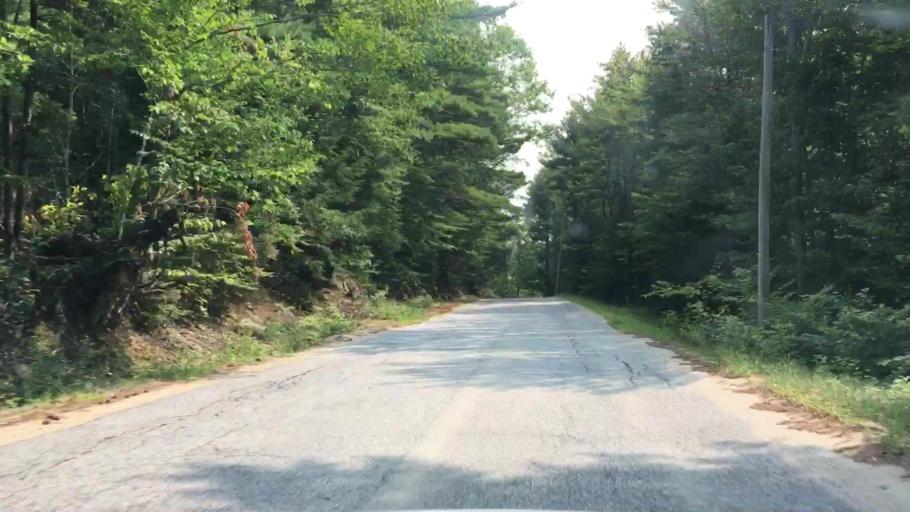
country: US
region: Maine
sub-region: Androscoggin County
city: Livermore
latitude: 44.3232
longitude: -70.2899
